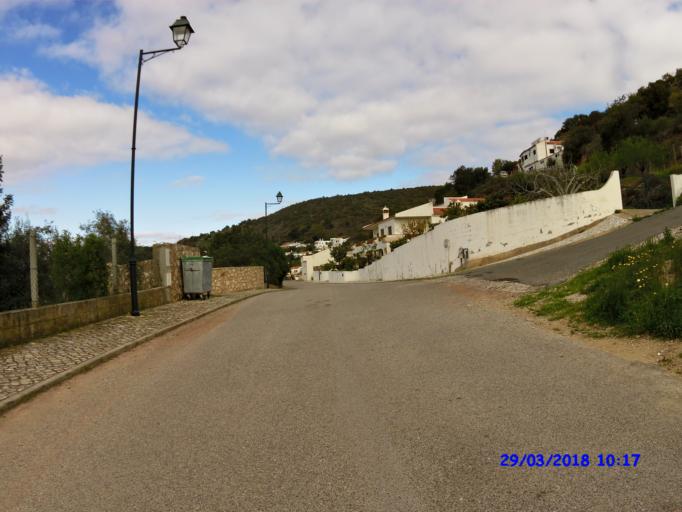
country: PT
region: Faro
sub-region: Loule
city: Boliqueime
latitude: 37.2348
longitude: -8.1710
